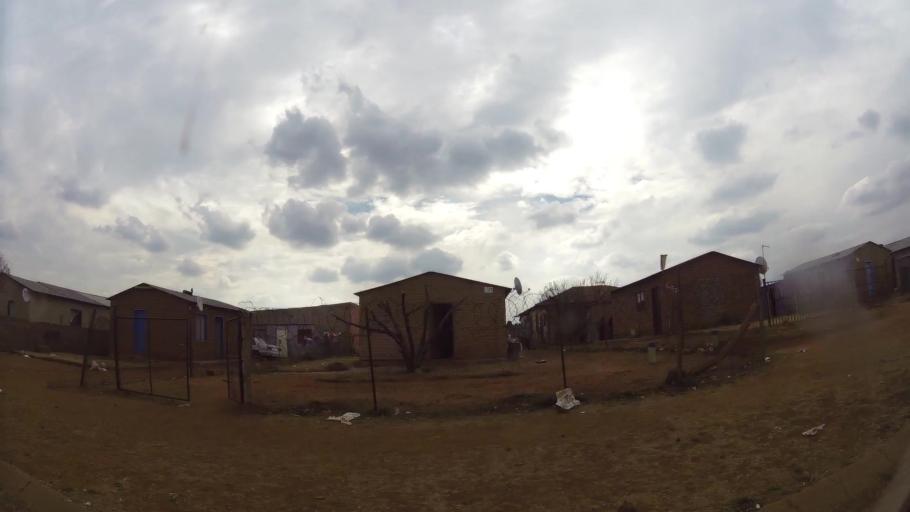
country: ZA
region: Gauteng
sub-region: Ekurhuleni Metropolitan Municipality
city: Germiston
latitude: -26.3878
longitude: 28.1186
